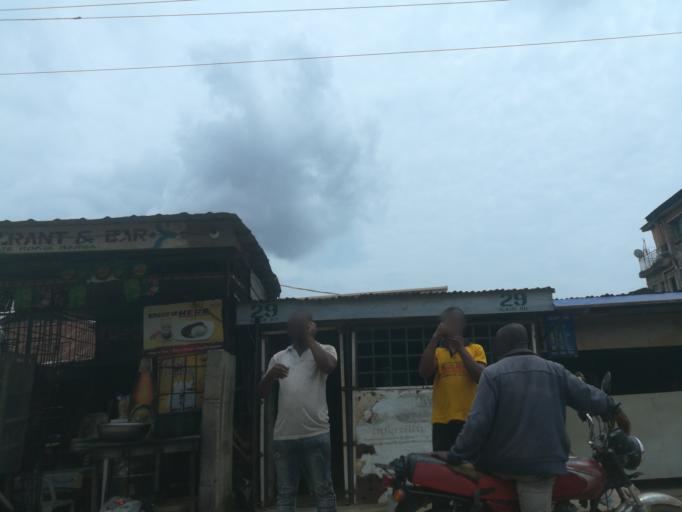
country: NG
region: Lagos
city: Somolu
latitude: 6.5326
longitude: 3.3932
